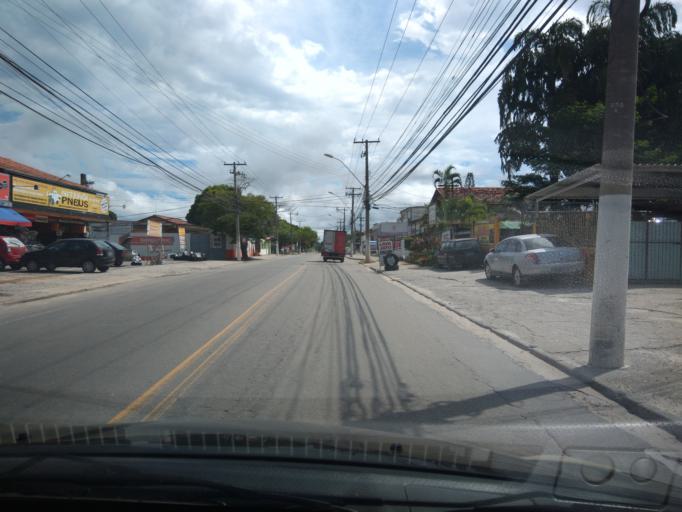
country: BR
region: Rio de Janeiro
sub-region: Niteroi
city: Niteroi
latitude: -22.9337
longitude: -43.0210
